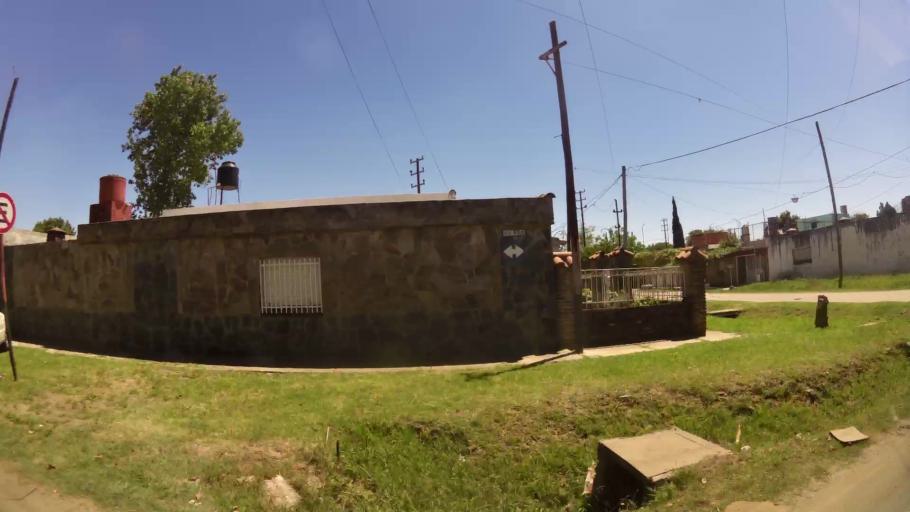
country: AR
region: Santa Fe
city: Perez
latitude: -32.9499
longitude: -60.7170
